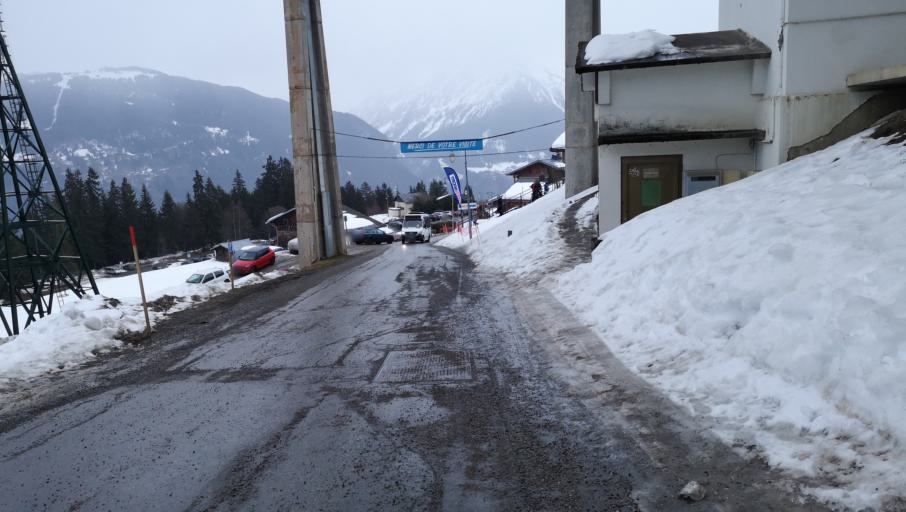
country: FR
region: Rhone-Alpes
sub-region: Departement de la Haute-Savoie
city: Saint-Gervais-les-Bains
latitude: 45.8750
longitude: 6.6856
